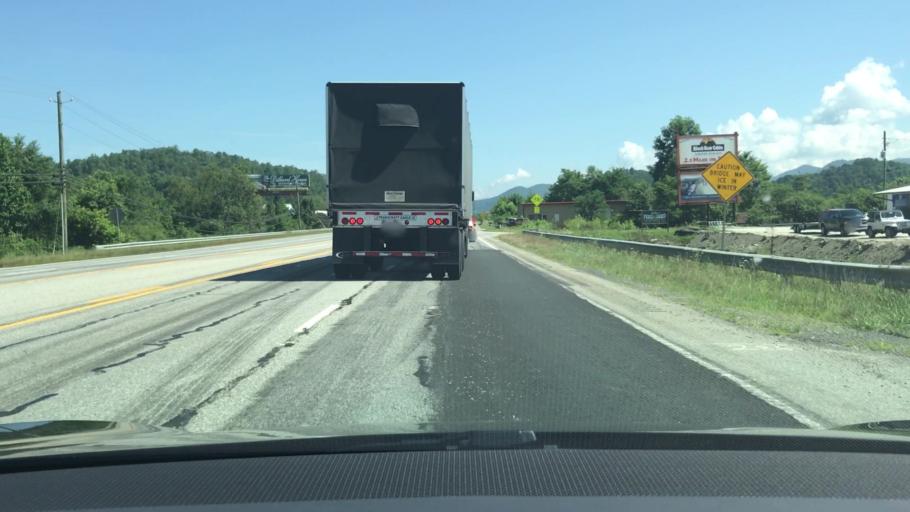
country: US
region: Georgia
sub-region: Rabun County
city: Mountain City
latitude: 34.9367
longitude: -83.3887
